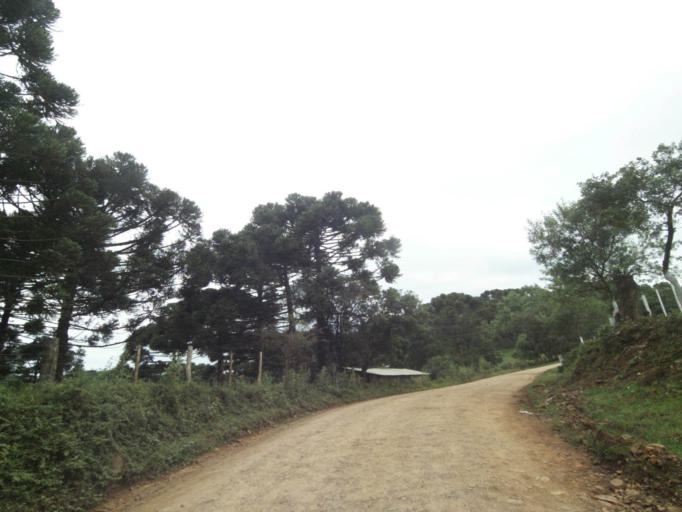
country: BR
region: Rio Grande do Sul
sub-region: Lagoa Vermelha
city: Lagoa Vermelha
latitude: -28.2105
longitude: -51.5029
